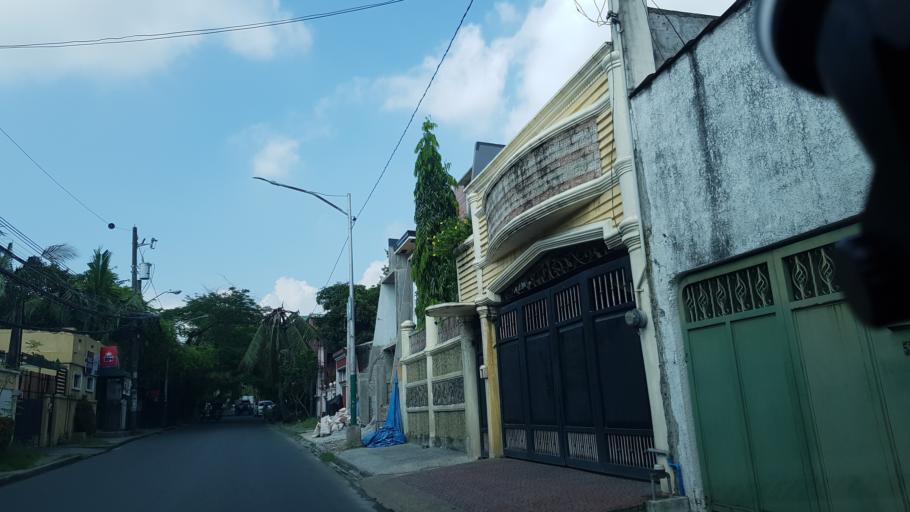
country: PH
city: Sambayanihan People's Village
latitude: 14.4763
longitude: 121.0275
